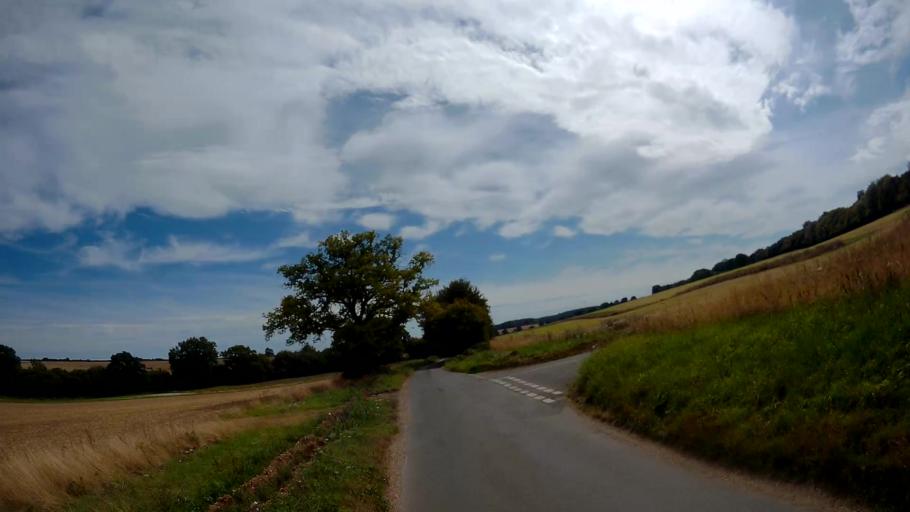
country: GB
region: England
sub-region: Hampshire
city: Odiham
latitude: 51.2373
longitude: -0.9711
